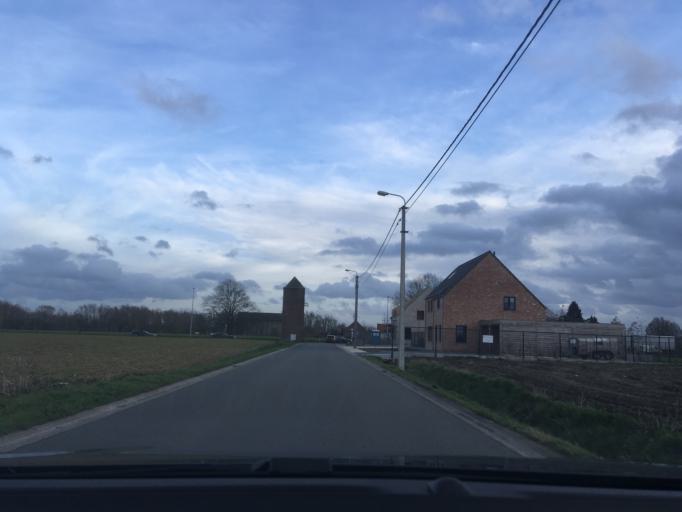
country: BE
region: Flanders
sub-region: Provincie West-Vlaanderen
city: Wielsbeke
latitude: 50.9010
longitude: 3.3488
